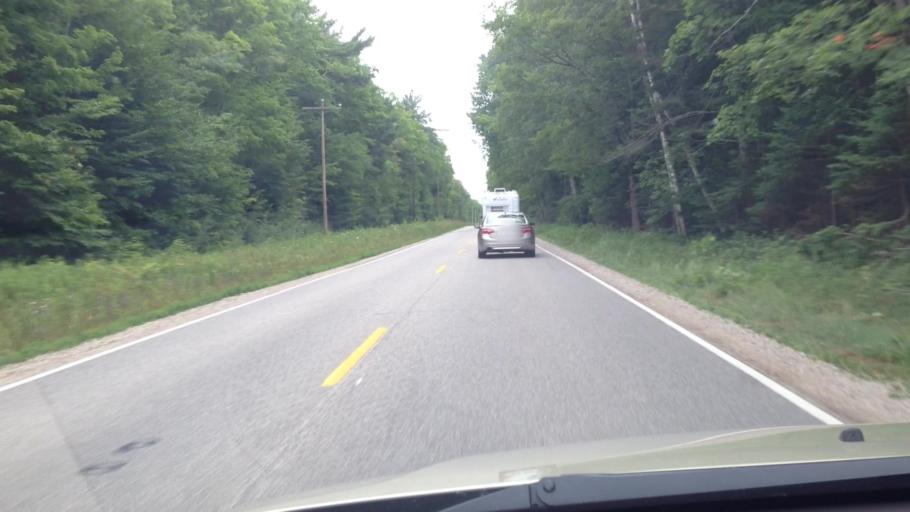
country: US
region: Michigan
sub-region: Mackinac County
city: Saint Ignace
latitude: 46.0568
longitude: -85.1469
